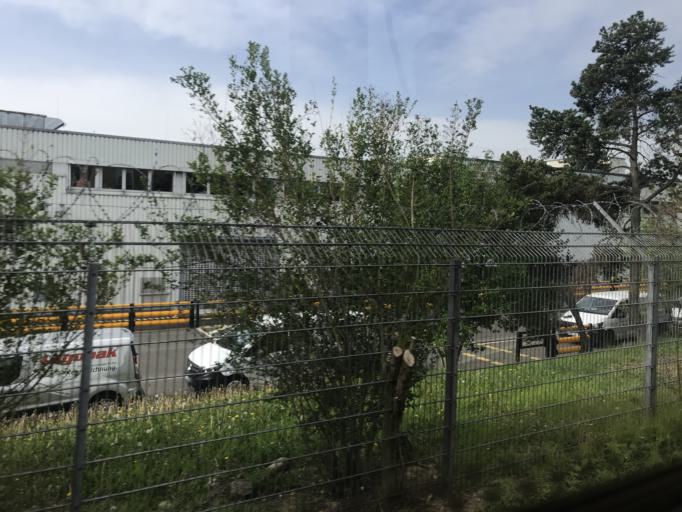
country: DE
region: Hesse
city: Liederbach
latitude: 50.1153
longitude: 8.5032
